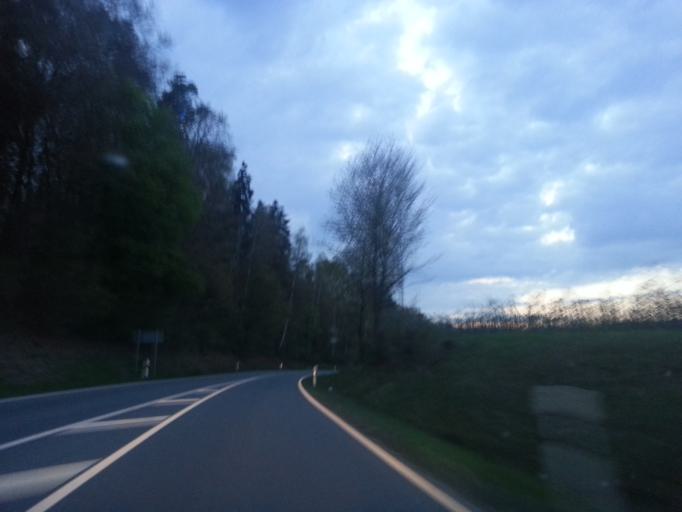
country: DE
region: Baden-Wuerttemberg
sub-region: Tuebingen Region
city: Oberteuringen
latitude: 47.6906
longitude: 9.4405
